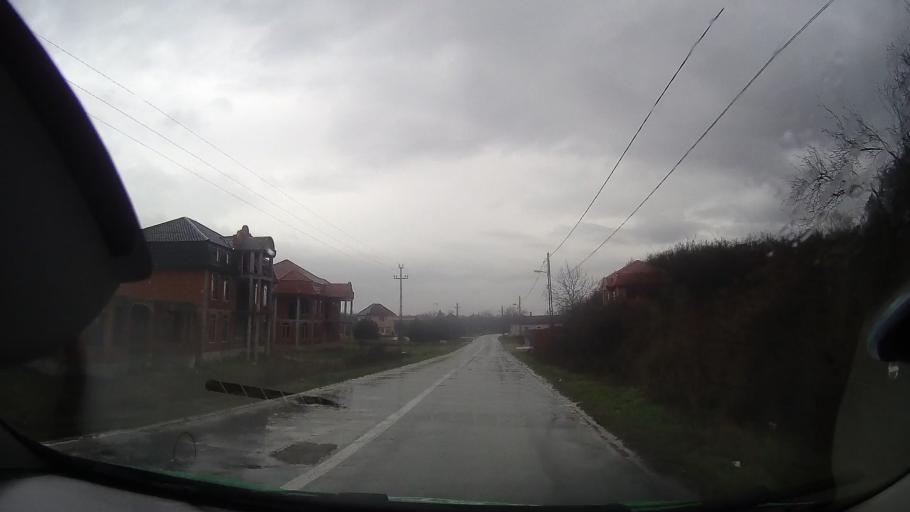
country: RO
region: Bihor
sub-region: Comuna Soimi
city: Soimi
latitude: 46.6832
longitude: 22.1147
